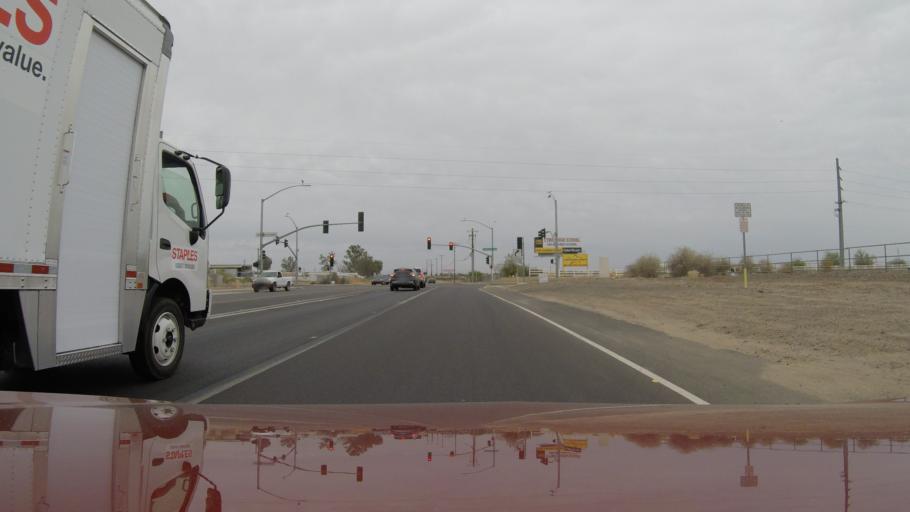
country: US
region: Arizona
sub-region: Maricopa County
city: Laveen
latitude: 33.3913
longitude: -112.2027
